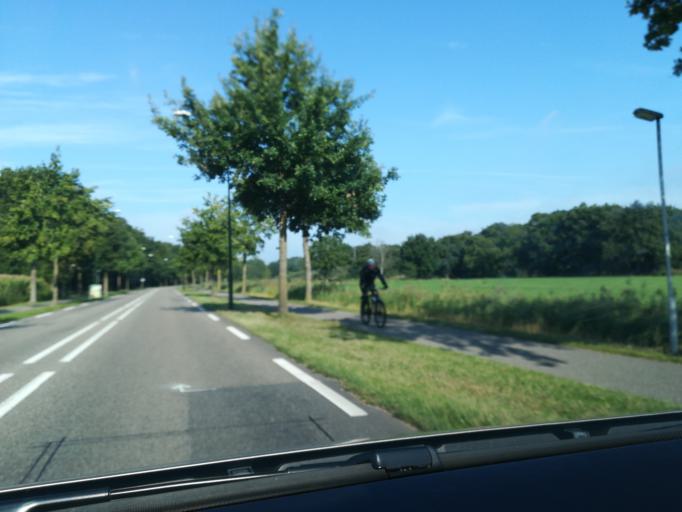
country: NL
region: North Brabant
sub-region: Gemeente Waalre
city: Waalre
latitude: 51.3993
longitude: 5.4314
